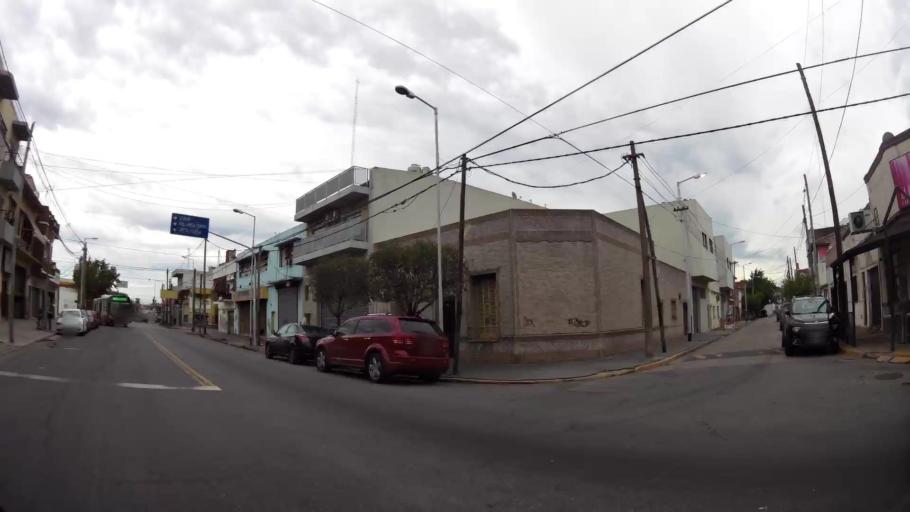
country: AR
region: Buenos Aires
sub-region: Partido de Lanus
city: Lanus
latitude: -34.6810
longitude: -58.3862
